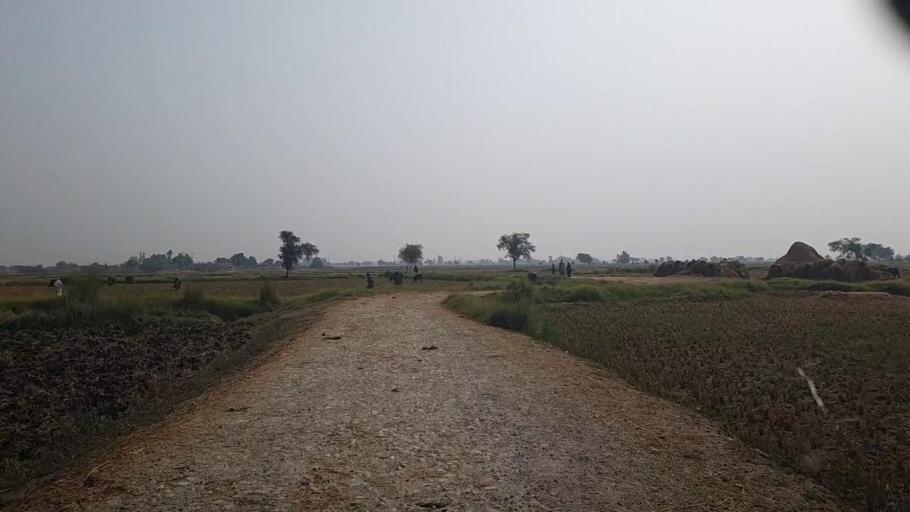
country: PK
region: Sindh
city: Kashmor
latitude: 28.3799
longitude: 69.4315
